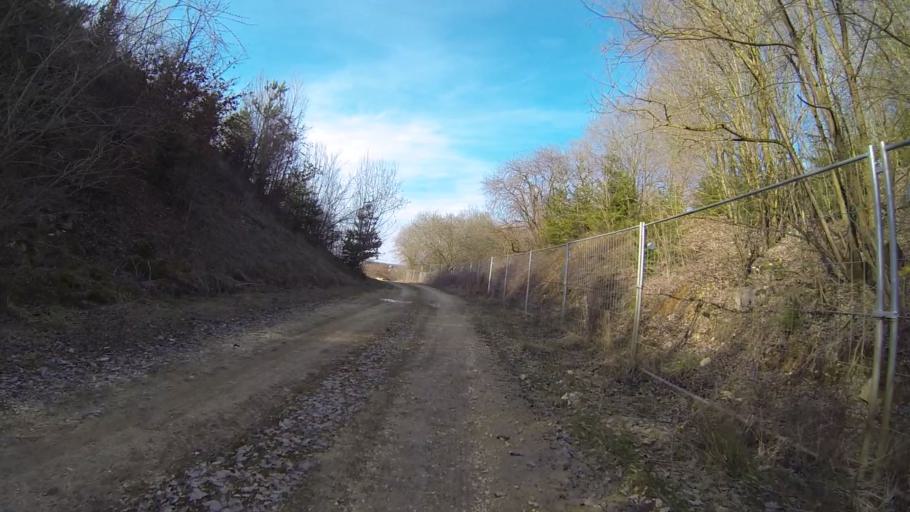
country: DE
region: Baden-Wuerttemberg
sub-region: Regierungsbezirk Stuttgart
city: Niederstotzingen
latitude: 48.5778
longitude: 10.2242
